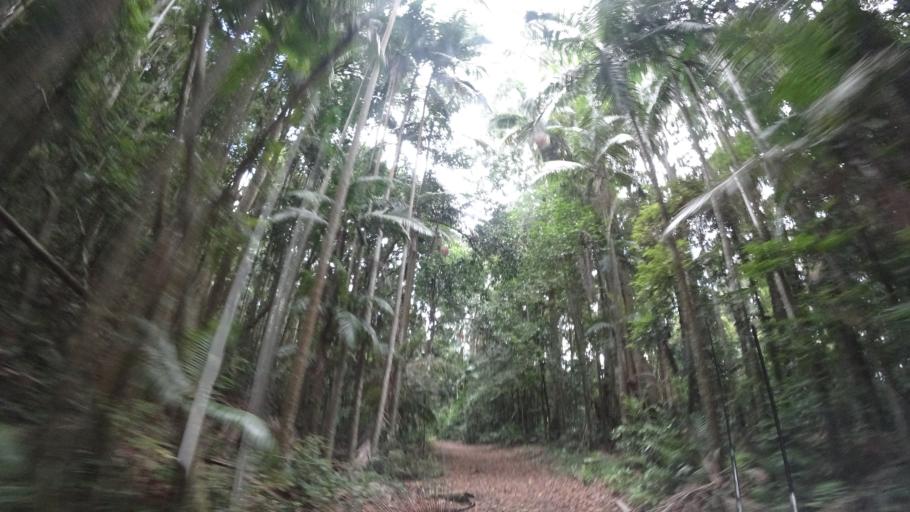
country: AU
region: Queensland
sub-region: Moreton Bay
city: Highvale
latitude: -27.3305
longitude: 152.7554
